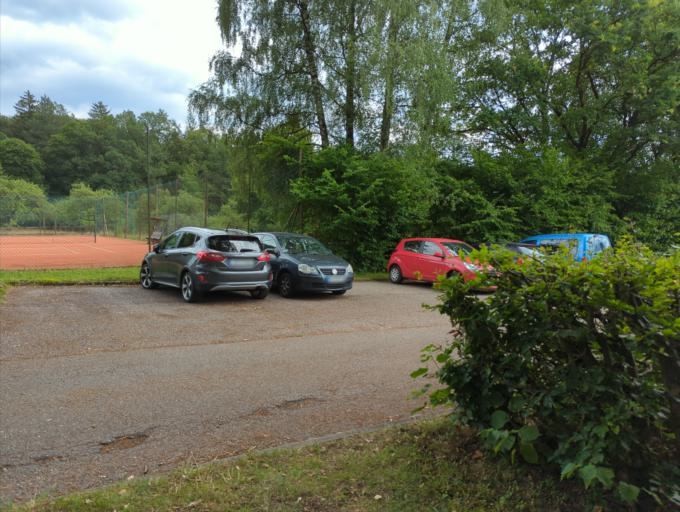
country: DE
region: Bavaria
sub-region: Upper Bavaria
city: Wasserburg am Inn
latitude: 48.0583
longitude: 12.2040
